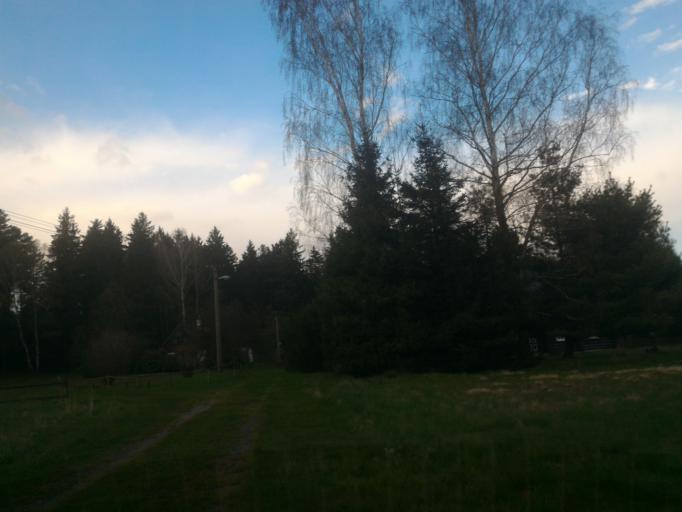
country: CZ
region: Ustecky
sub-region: Okres Decin
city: Chribska
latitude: 50.8922
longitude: 14.4612
